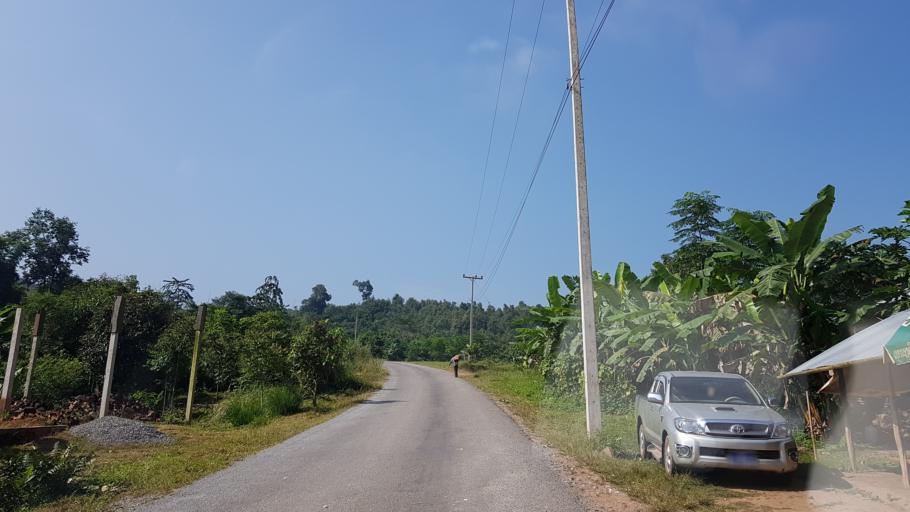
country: LA
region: Oudomxai
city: Muang Xay
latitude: 20.7148
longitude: 102.0872
